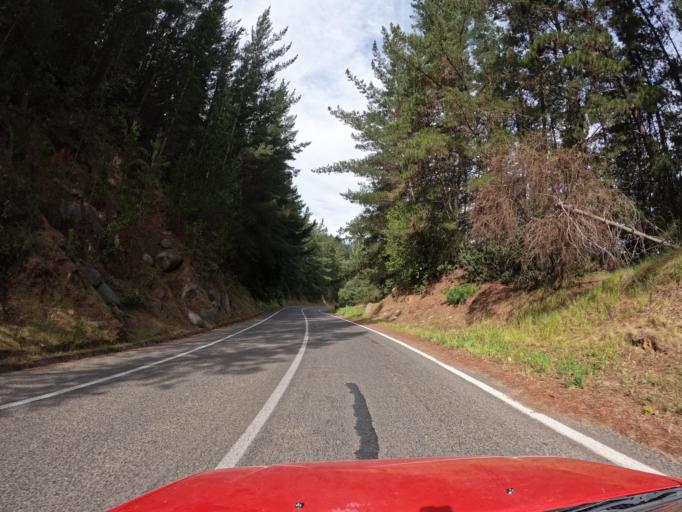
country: CL
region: Maule
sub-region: Provincia de Talca
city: Talca
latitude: -35.2974
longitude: -71.9681
